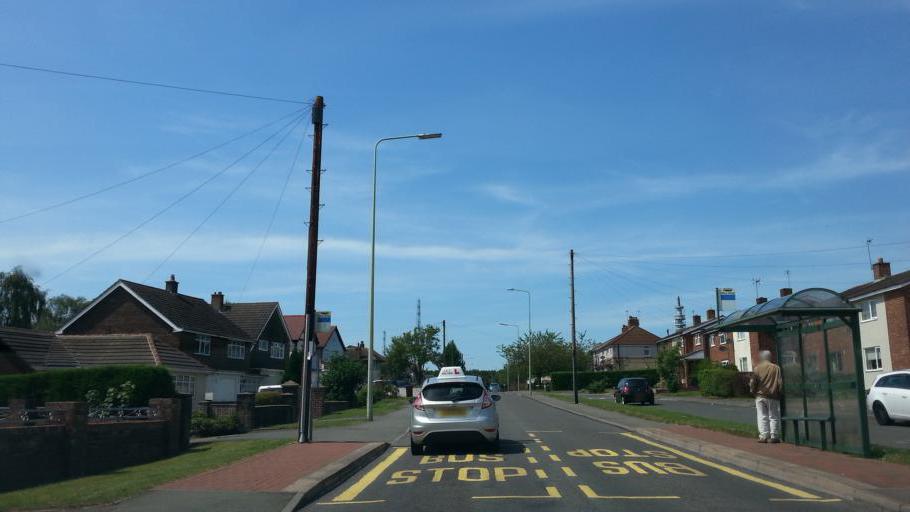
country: GB
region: England
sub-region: Staffordshire
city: Cannock
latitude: 52.7229
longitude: -2.0132
